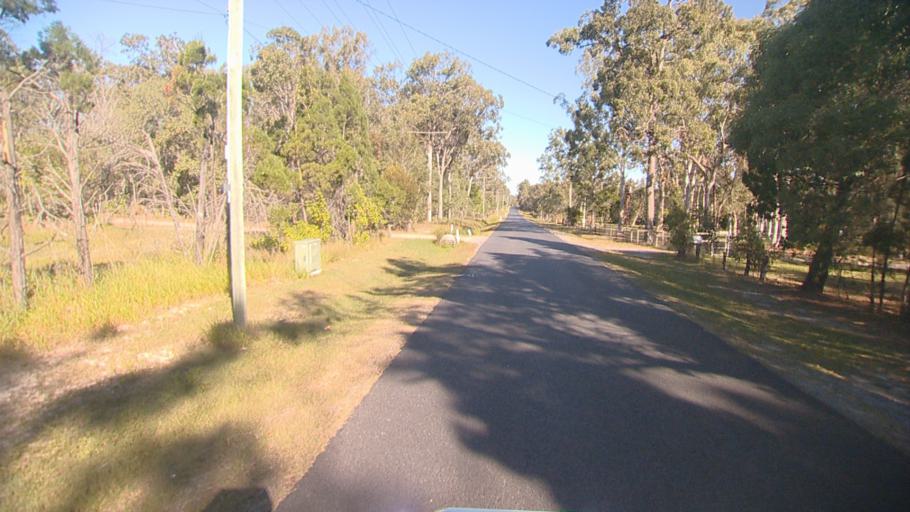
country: AU
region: Queensland
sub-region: Logan
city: Logan Reserve
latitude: -27.7268
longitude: 153.0729
